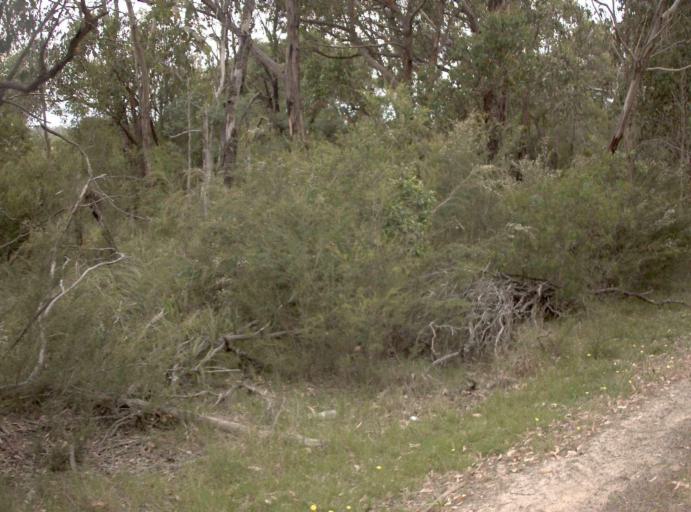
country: AU
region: Victoria
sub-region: Latrobe
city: Traralgon
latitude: -38.5092
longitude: 146.8484
